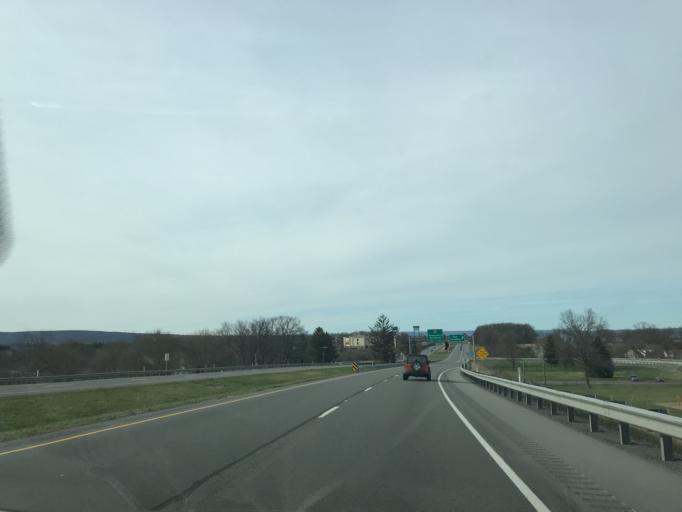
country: US
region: Pennsylvania
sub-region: Union County
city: New Columbia
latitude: 41.0393
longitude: -76.8707
